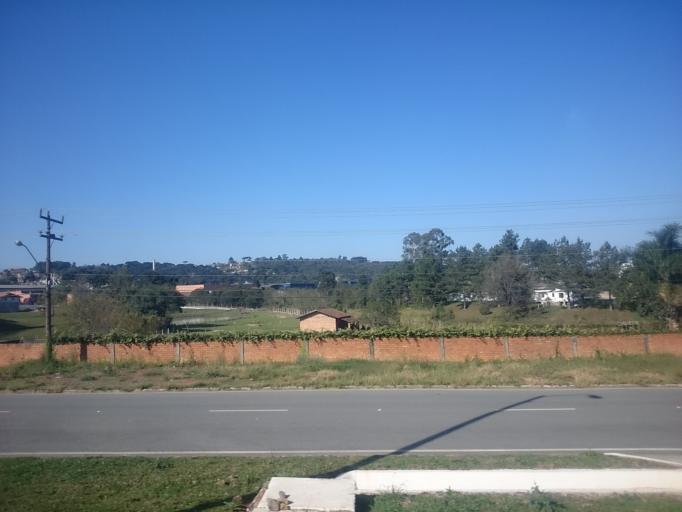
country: BR
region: Parana
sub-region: Rio Negro
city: Rio Negro
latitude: -26.0907
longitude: -49.7801
